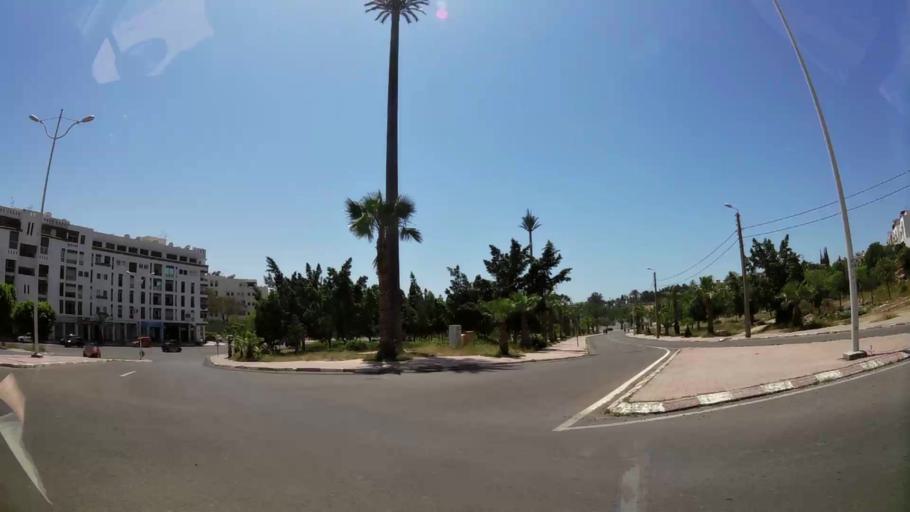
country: MA
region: Souss-Massa-Draa
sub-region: Agadir-Ida-ou-Tnan
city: Agadir
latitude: 30.4292
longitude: -9.5909
